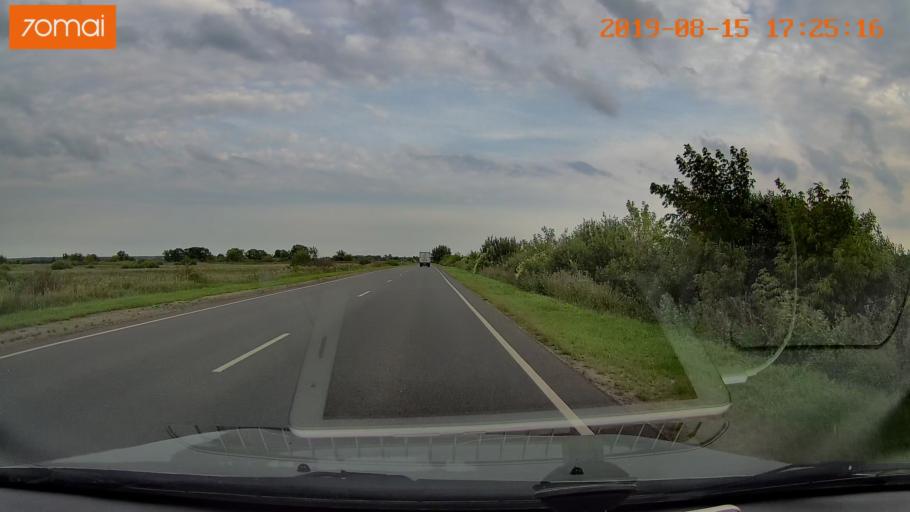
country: RU
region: Moskovskaya
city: Ashitkovo
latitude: 55.3768
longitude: 38.5638
